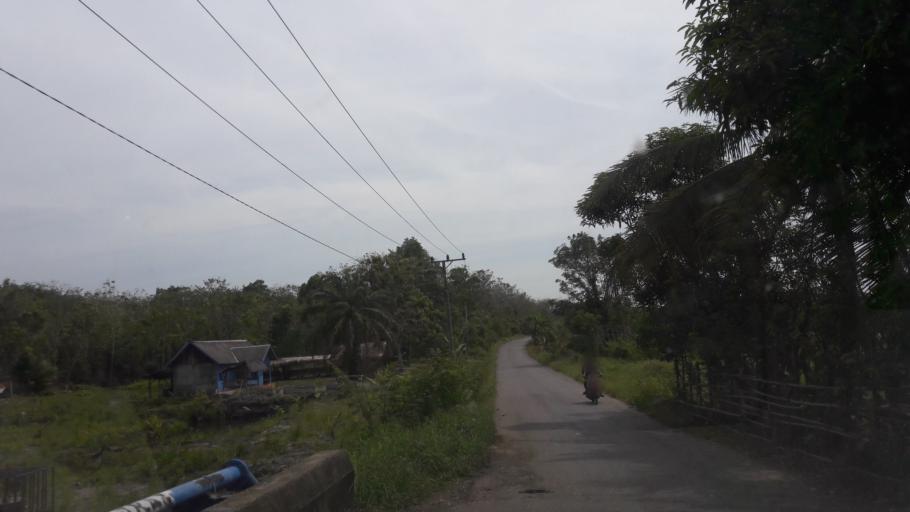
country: ID
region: South Sumatra
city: Gunungmenang
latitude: -3.1381
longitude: 104.1131
